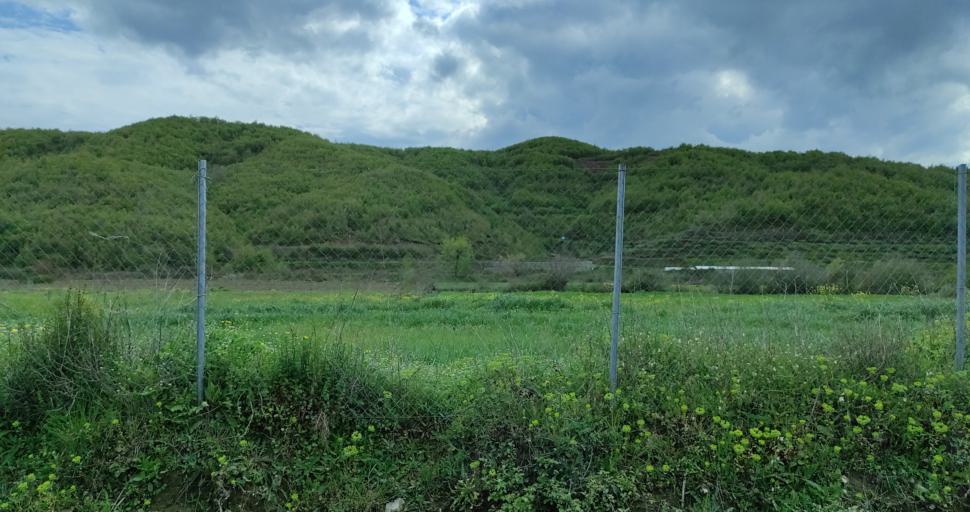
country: AL
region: Shkoder
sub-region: Rrethi i Shkodres
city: Dajc
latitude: 42.0354
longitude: 19.4036
